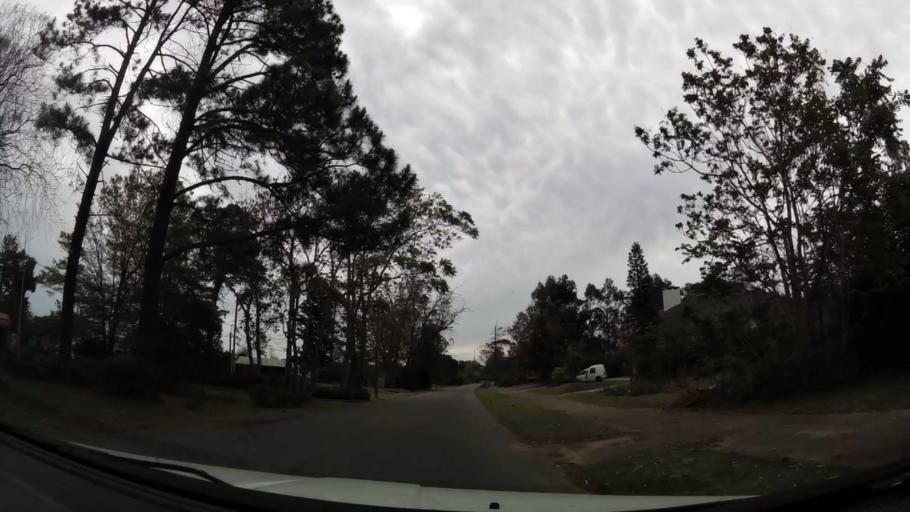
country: UY
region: Maldonado
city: Maldonado
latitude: -34.9082
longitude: -54.9927
